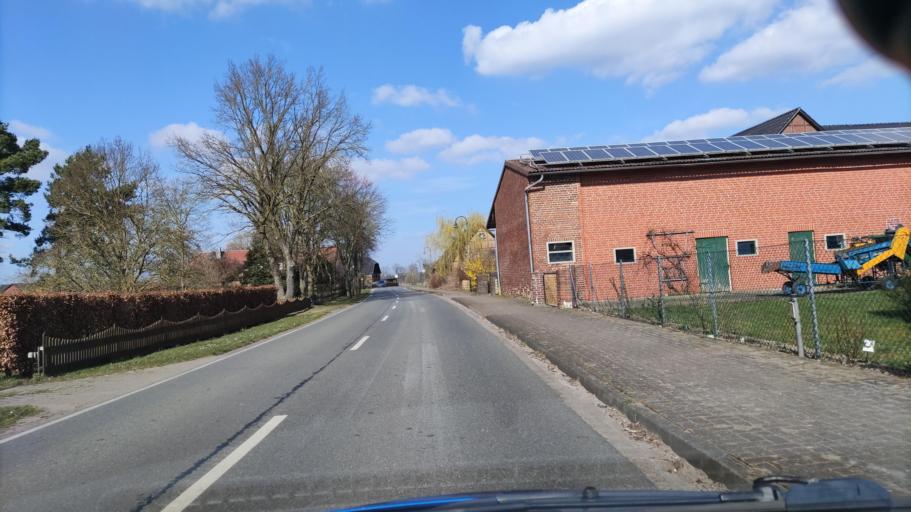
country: DE
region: Lower Saxony
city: Trebel
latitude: 53.0058
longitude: 11.2534
